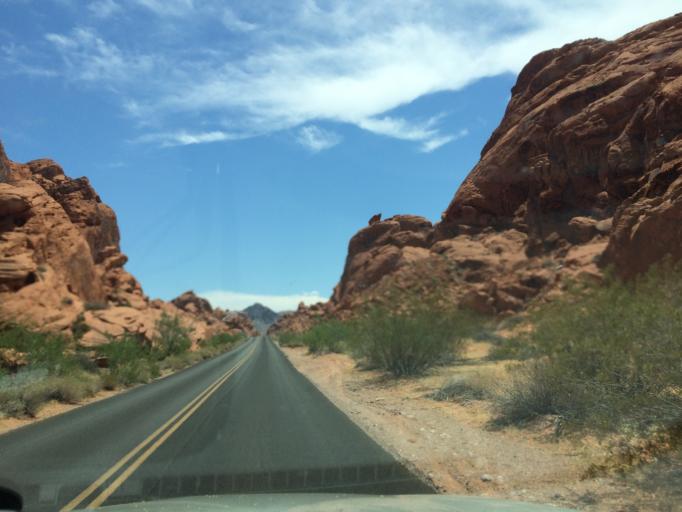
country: US
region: Nevada
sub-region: Clark County
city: Moapa Valley
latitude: 36.4457
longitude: -114.5161
